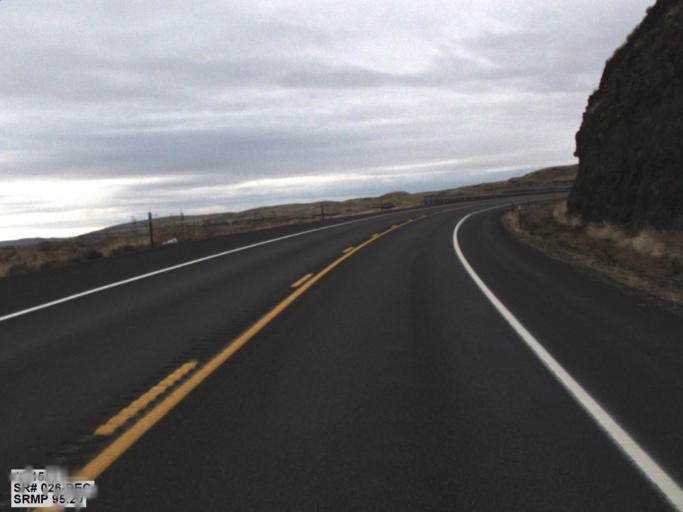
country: US
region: Washington
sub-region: Adams County
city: Ritzville
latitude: 46.7771
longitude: -118.0767
